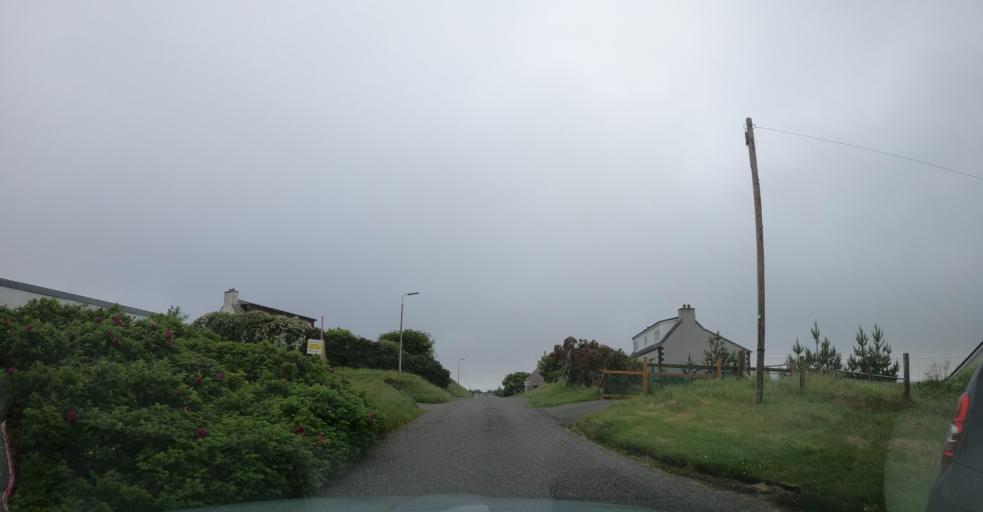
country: GB
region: Scotland
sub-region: Eilean Siar
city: Stornoway
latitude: 58.1961
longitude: -6.2235
